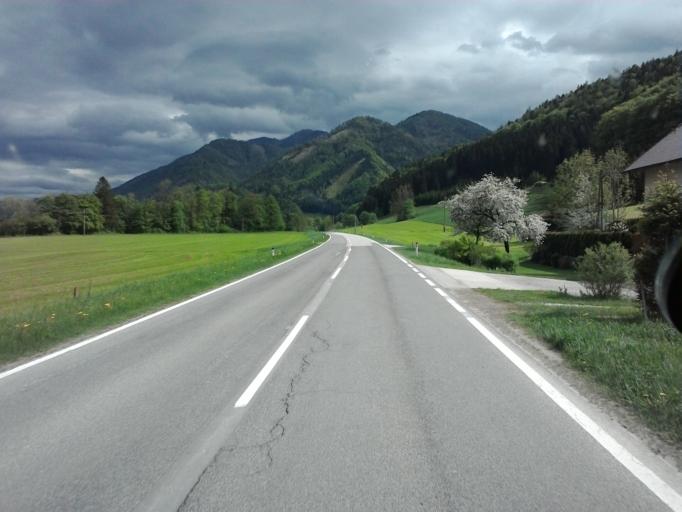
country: AT
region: Upper Austria
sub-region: Politischer Bezirk Kirchdorf an der Krems
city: Micheldorf in Oberoesterreich
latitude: 47.7805
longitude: 14.1618
